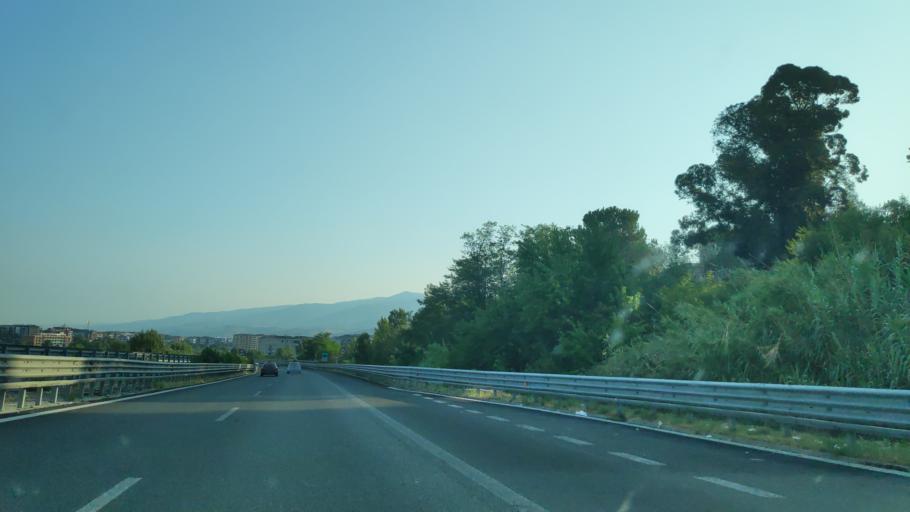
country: IT
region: Calabria
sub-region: Provincia di Cosenza
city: Cosenza
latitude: 39.3130
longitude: 16.2401
